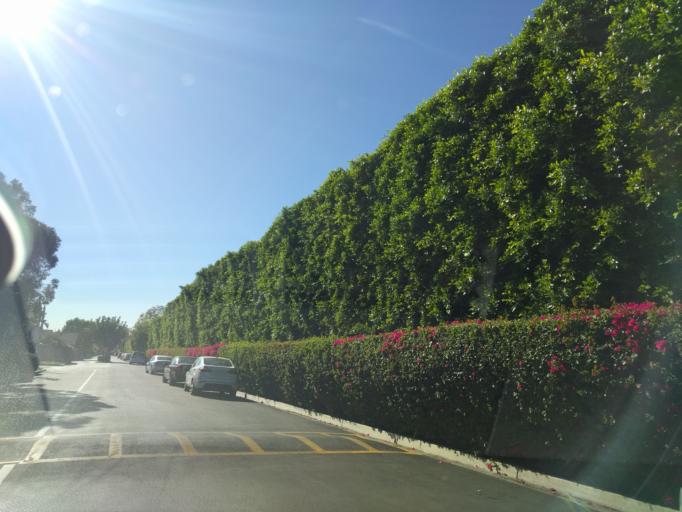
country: US
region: California
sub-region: Orange County
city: Irvine
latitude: 33.7065
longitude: -117.7829
